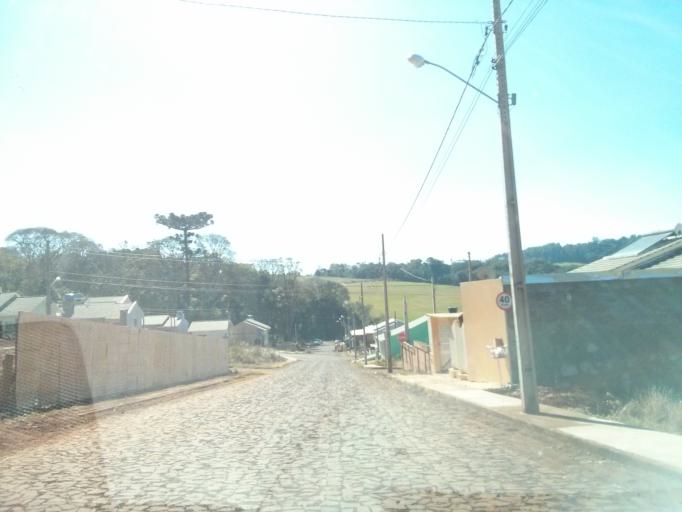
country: BR
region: Santa Catarina
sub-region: Chapeco
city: Chapeco
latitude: -27.0896
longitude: -52.6884
